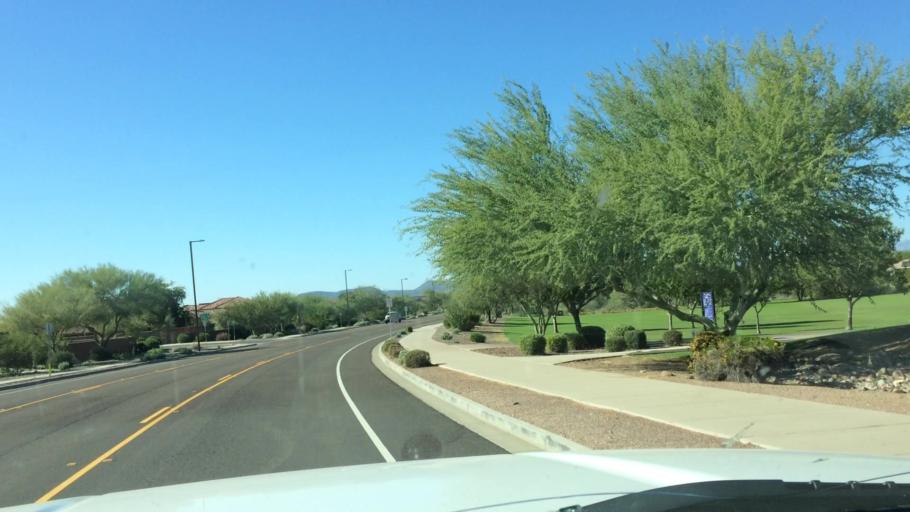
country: US
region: Arizona
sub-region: Maricopa County
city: Anthem
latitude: 33.8469
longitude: -112.1022
